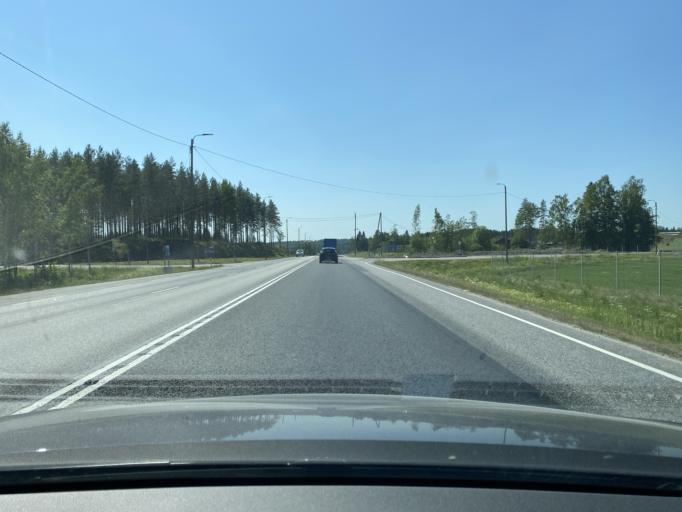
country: FI
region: Pirkanmaa
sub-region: Lounais-Pirkanmaa
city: Mouhijaervi
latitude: 61.3690
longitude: 23.1263
